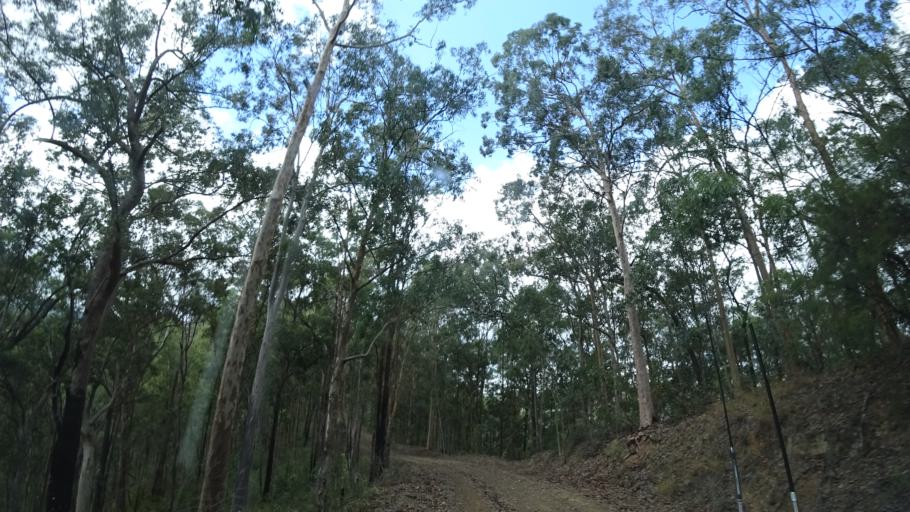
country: AU
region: Queensland
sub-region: Moreton Bay
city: Highvale
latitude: -27.3572
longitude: 152.7375
